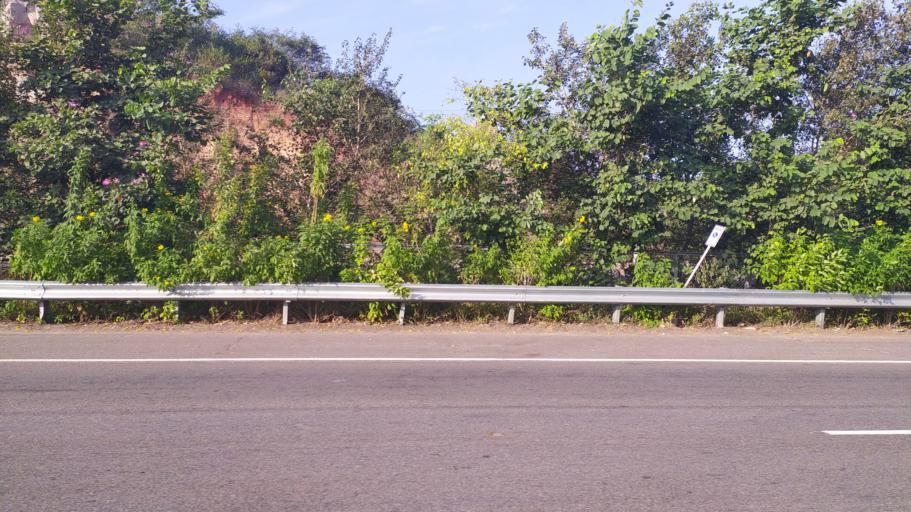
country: IN
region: Telangana
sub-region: Hyderabad
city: Hyderabad
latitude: 17.3654
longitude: 78.3520
